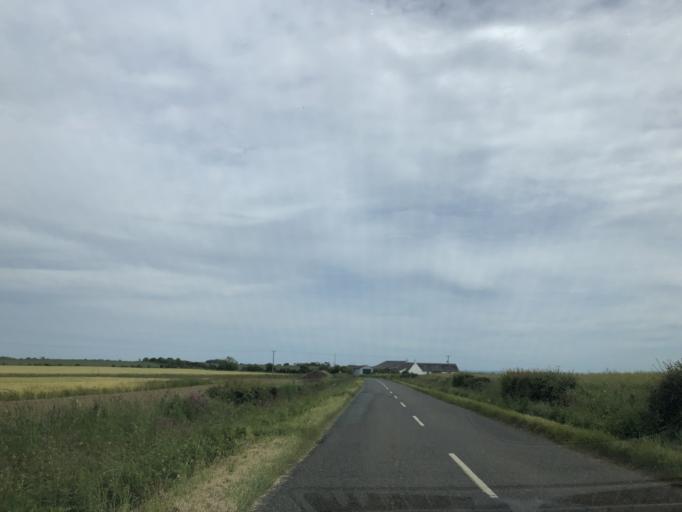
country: GB
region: Scotland
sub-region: Fife
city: Anstruther
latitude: 56.2595
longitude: -2.6862
